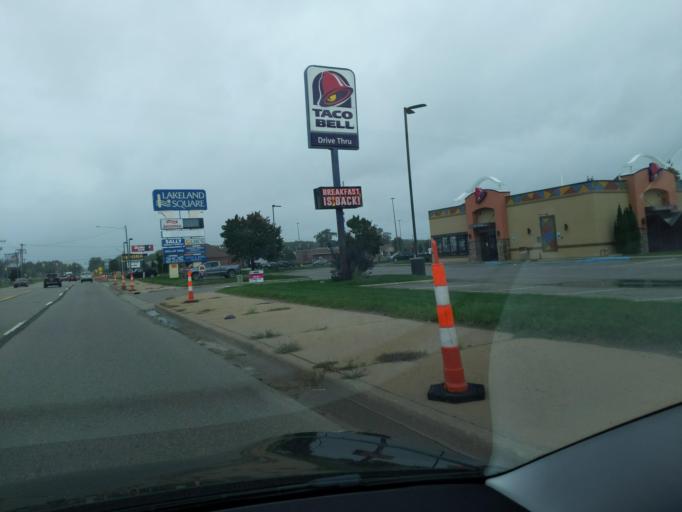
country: US
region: Michigan
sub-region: Wexford County
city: Cadillac
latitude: 44.2792
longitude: -85.4066
